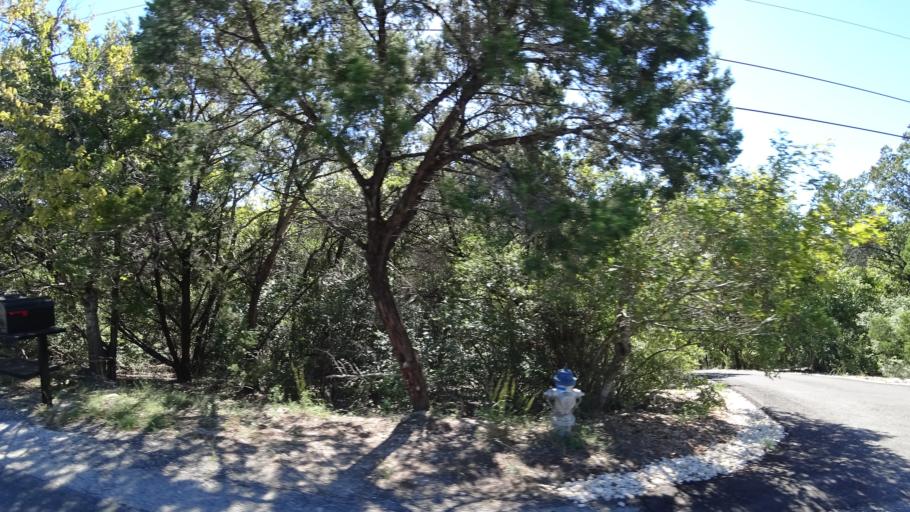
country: US
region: Texas
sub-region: Travis County
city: West Lake Hills
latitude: 30.3069
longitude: -97.8115
